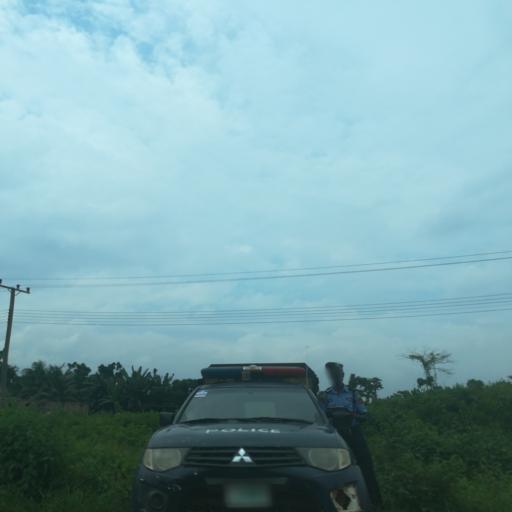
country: NG
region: Lagos
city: Ejirin
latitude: 6.6472
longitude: 3.7681
